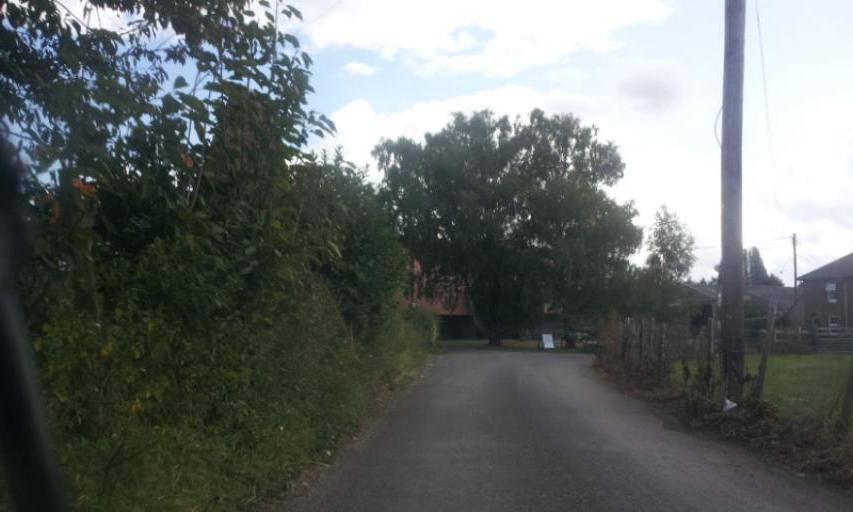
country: GB
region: England
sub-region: Kent
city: Newington
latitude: 51.3405
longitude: 0.6660
